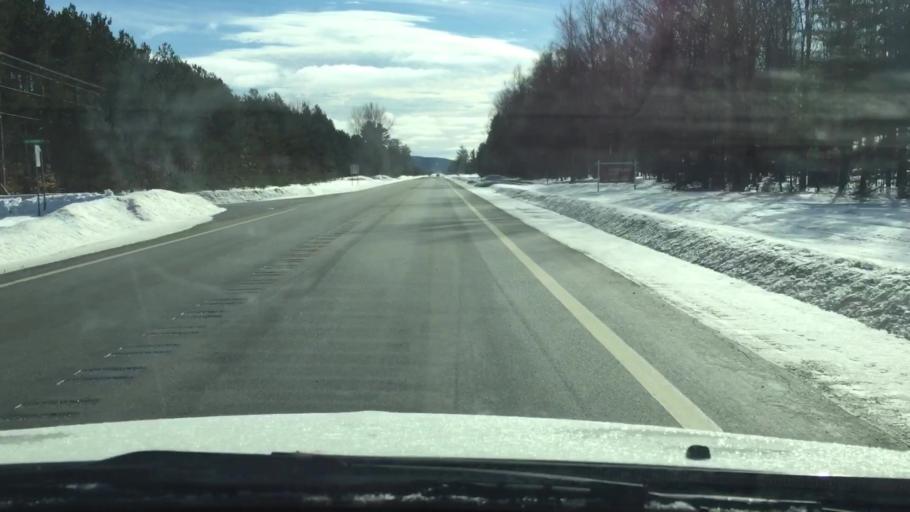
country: US
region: Michigan
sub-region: Antrim County
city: Mancelona
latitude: 44.9390
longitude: -85.0508
